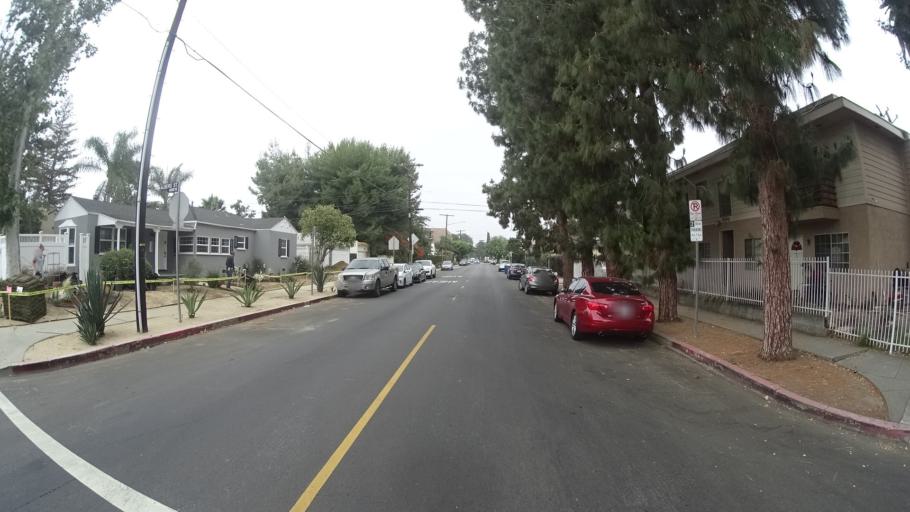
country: US
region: California
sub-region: Los Angeles County
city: Van Nuys
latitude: 34.1704
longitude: -118.4509
